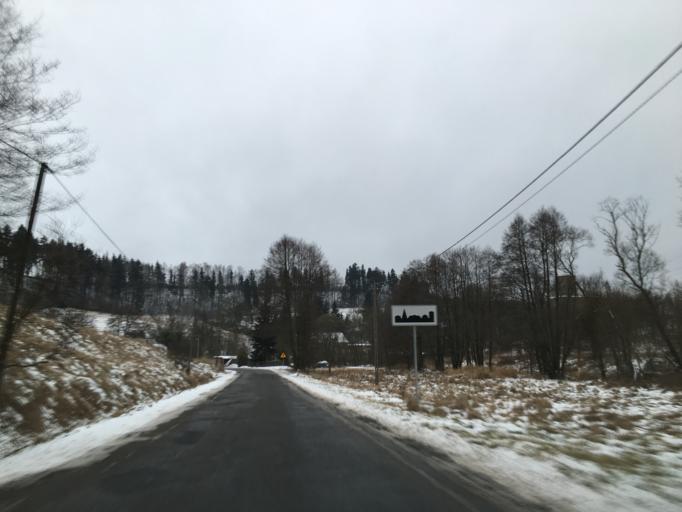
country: CZ
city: Radvanice
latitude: 50.6325
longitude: 16.0437
